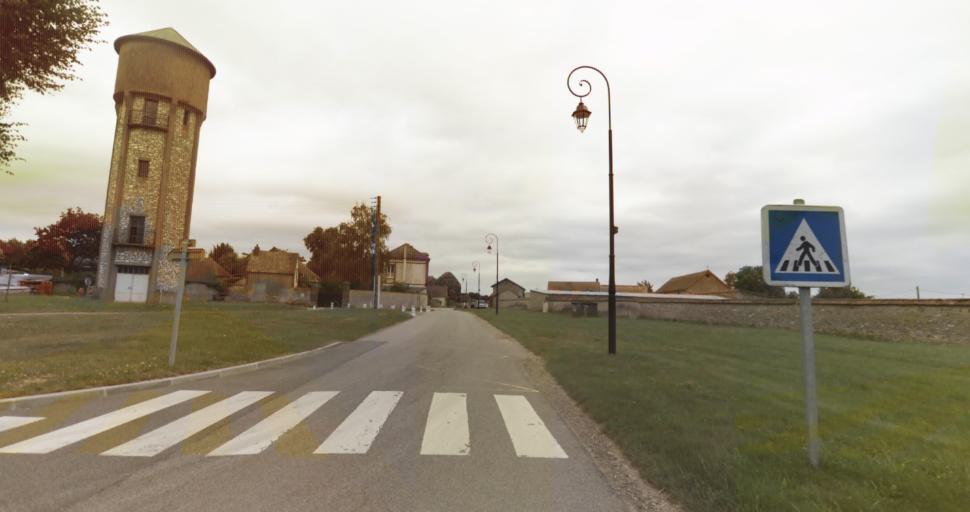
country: FR
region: Haute-Normandie
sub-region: Departement de l'Eure
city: La Couture-Boussey
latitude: 48.9337
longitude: 1.3979
